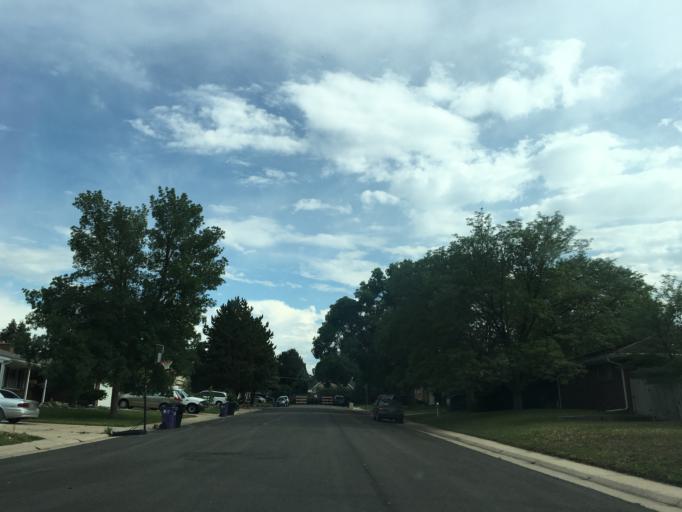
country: US
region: Colorado
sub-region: Jefferson County
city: Lakewood
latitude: 39.6764
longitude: -105.0621
